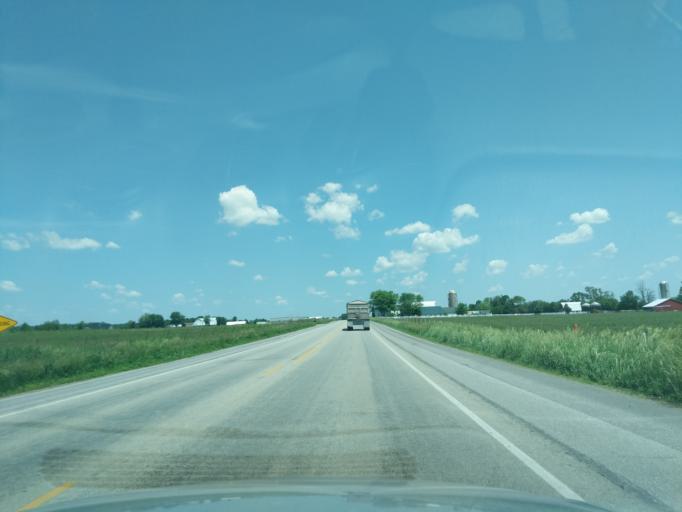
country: US
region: Indiana
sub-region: LaGrange County
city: Topeka
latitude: 41.5770
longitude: -85.5786
